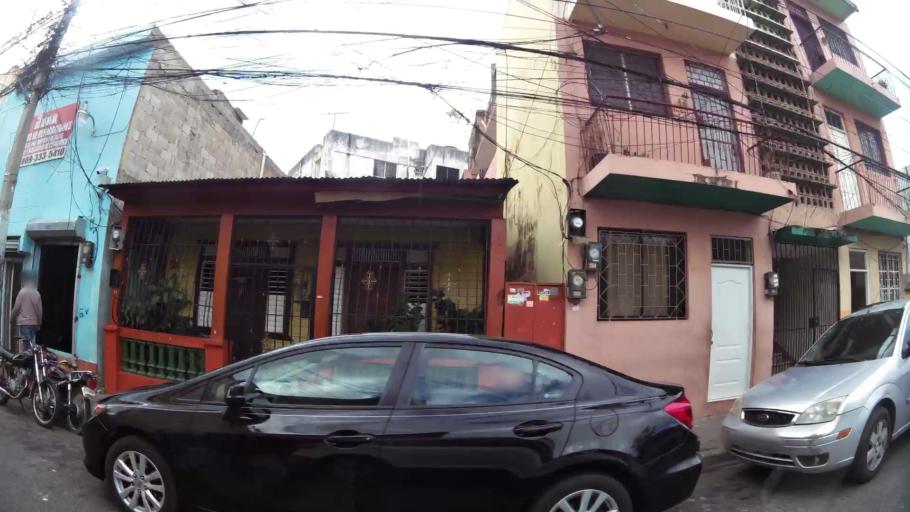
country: DO
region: Nacional
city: San Carlos
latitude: 18.4792
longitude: -69.8964
